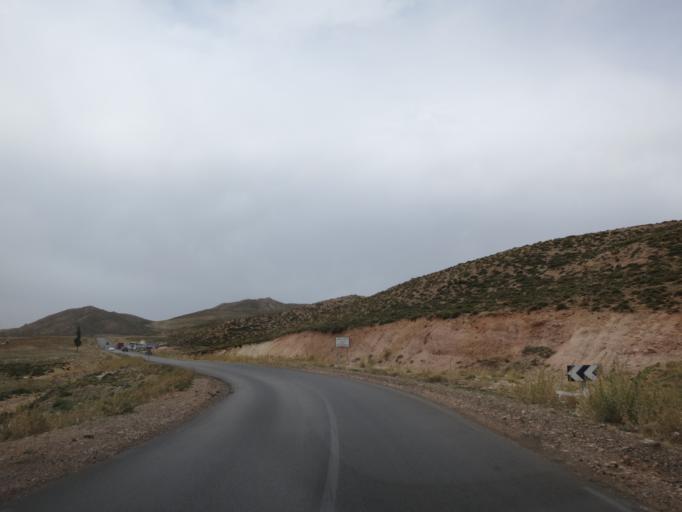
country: MA
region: Meknes-Tafilalet
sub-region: Khenifra
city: Itzer
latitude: 33.0460
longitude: -5.0499
